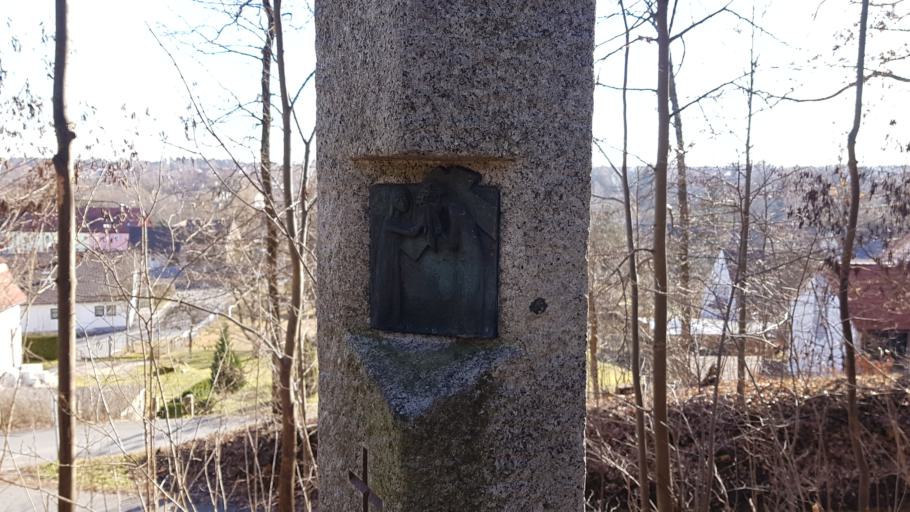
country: DE
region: Bavaria
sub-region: Upper Palatinate
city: Grafenwohr
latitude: 49.7211
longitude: 11.9005
